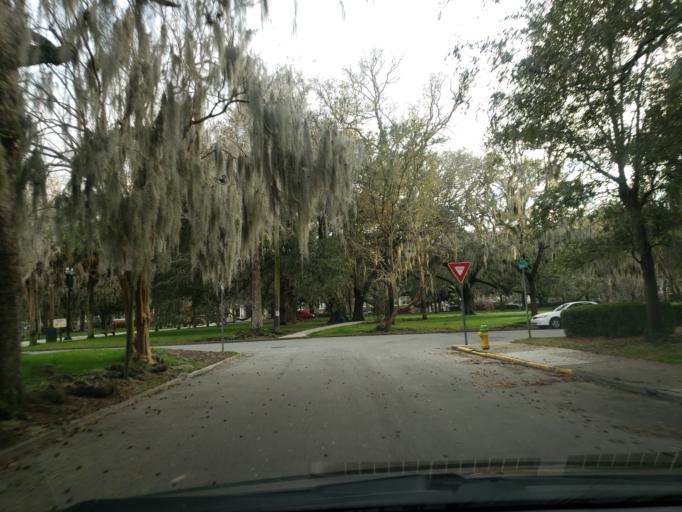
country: US
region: Georgia
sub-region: Chatham County
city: Savannah
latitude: 32.0478
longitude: -81.0924
